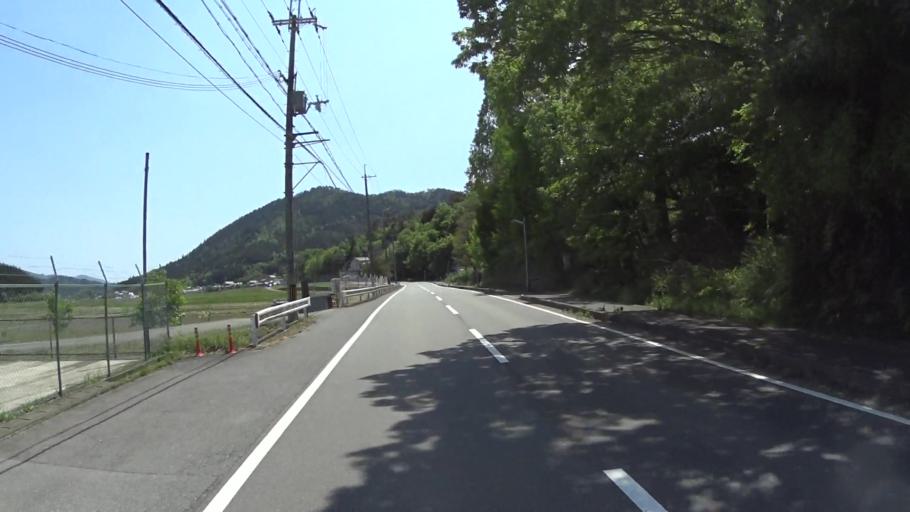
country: JP
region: Kyoto
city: Kameoka
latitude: 35.0321
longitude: 135.4841
